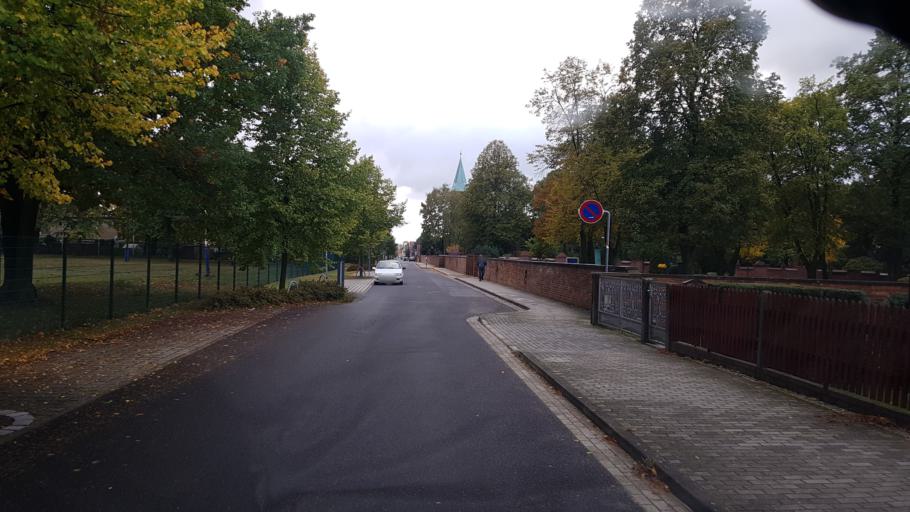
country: DE
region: Brandenburg
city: Grossraschen
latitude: 51.5936
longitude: 14.0092
